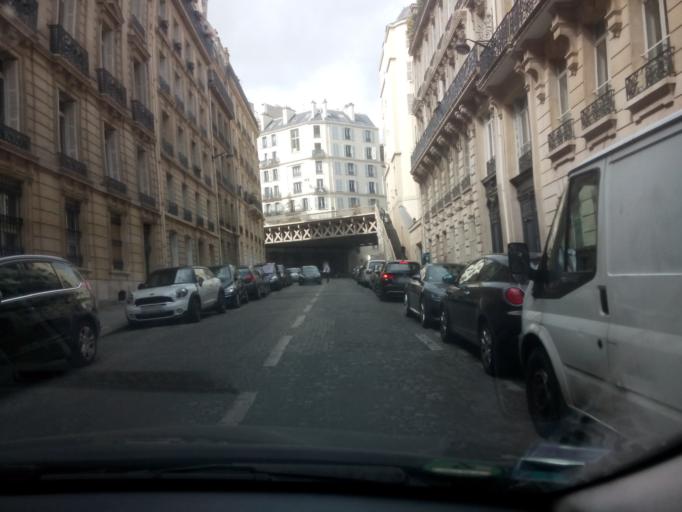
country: FR
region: Ile-de-France
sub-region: Departement des Hauts-de-Seine
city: Clichy
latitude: 48.8772
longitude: 2.3197
